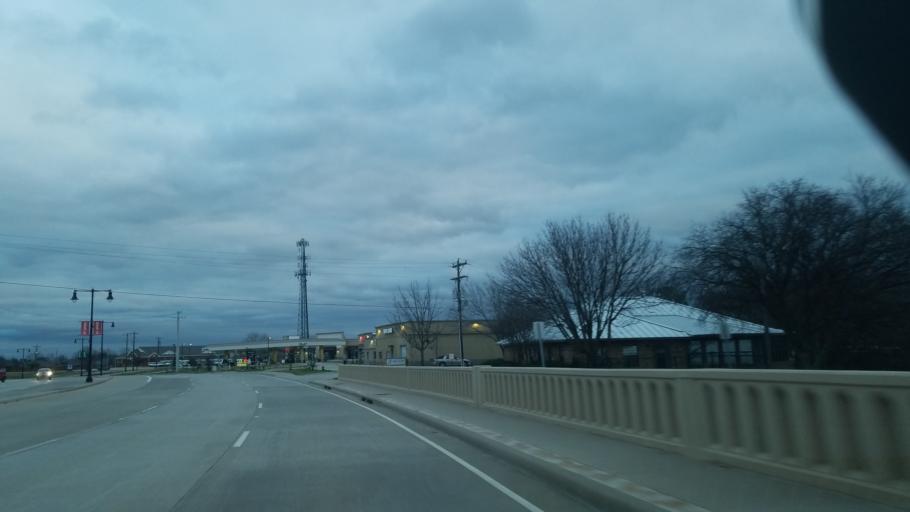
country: US
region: Texas
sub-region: Denton County
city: Little Elm
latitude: 33.1557
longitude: -96.9506
